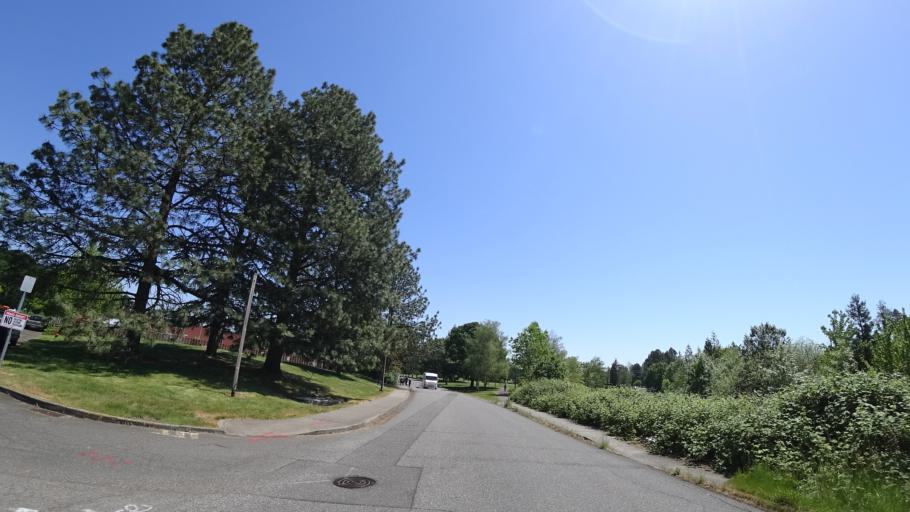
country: US
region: Oregon
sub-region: Washington County
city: Beaverton
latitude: 45.4967
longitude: -122.8221
